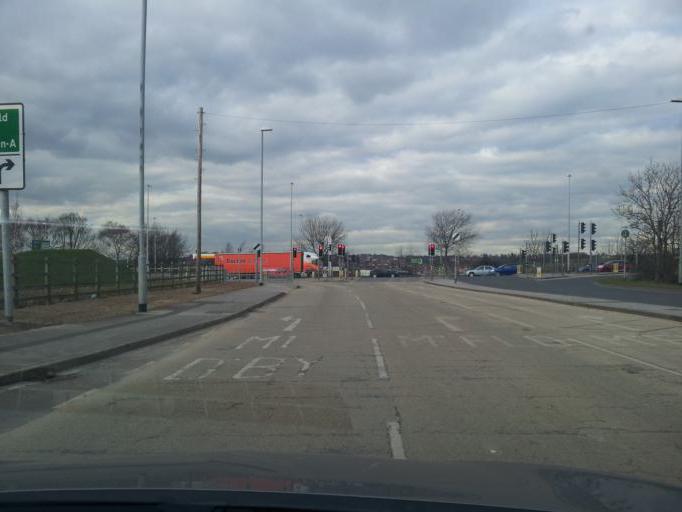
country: GB
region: England
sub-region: Derbyshire
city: Pinxton
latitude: 53.1108
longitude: -1.2964
